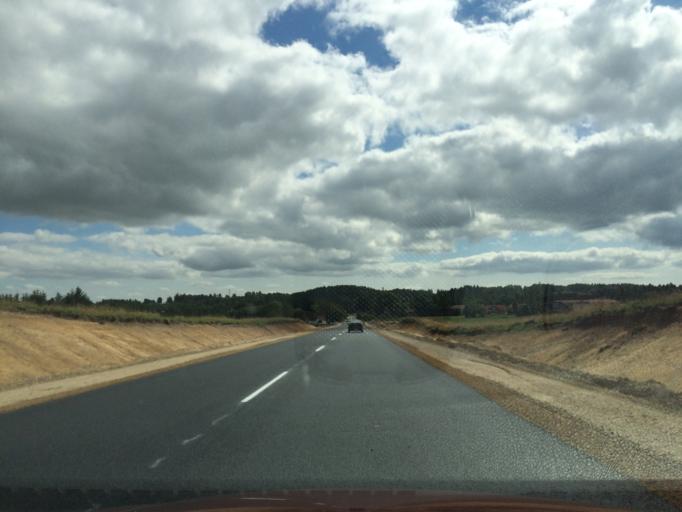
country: DK
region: Central Jutland
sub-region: Silkeborg Kommune
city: Svejbaek
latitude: 56.1847
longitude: 9.6363
